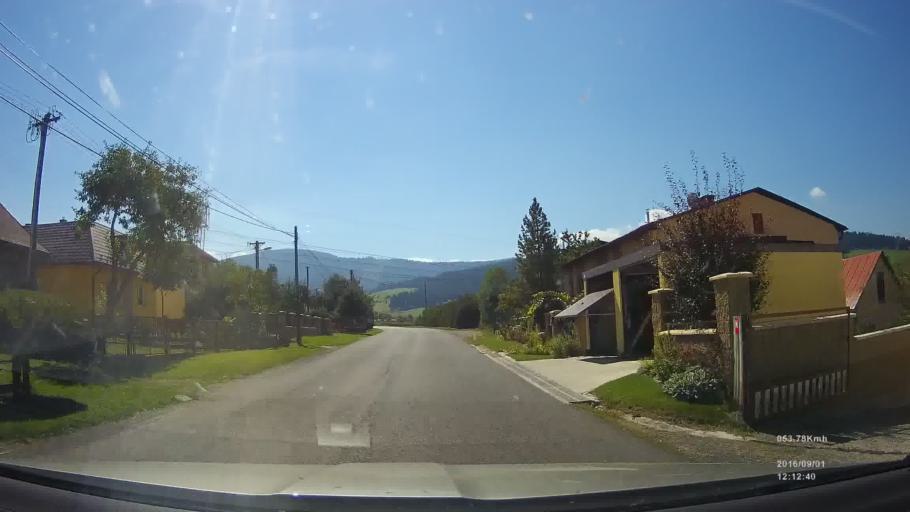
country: SK
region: Zilinsky
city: Ruzomberok
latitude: 49.0560
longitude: 19.4308
